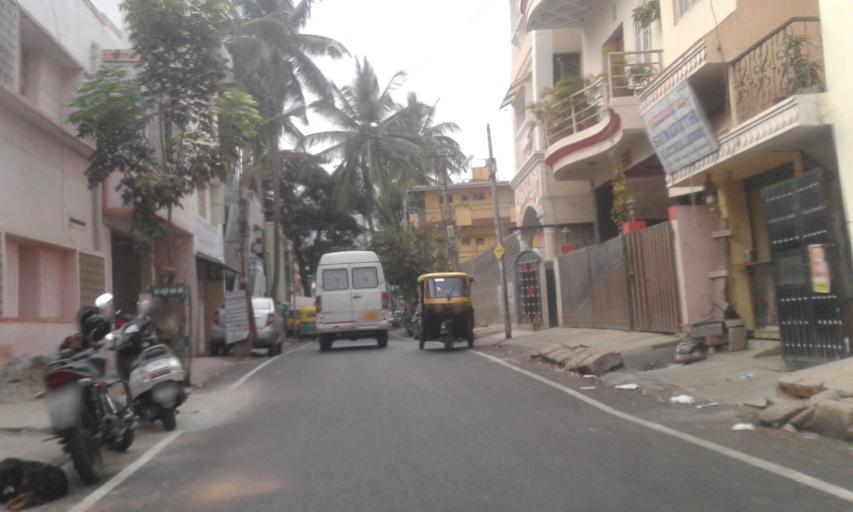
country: IN
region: Karnataka
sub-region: Bangalore Urban
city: Bangalore
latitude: 12.9355
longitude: 77.5908
